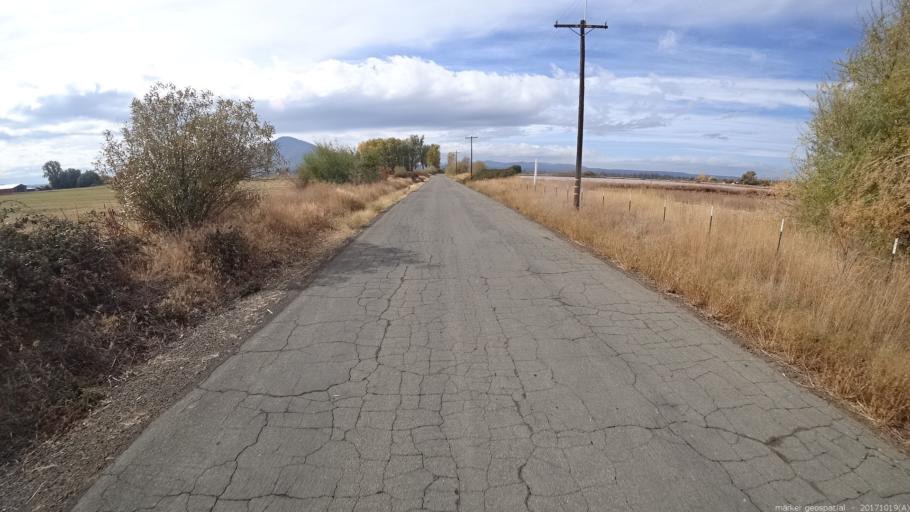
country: US
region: California
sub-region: Shasta County
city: Burney
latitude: 41.0979
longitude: -121.4887
